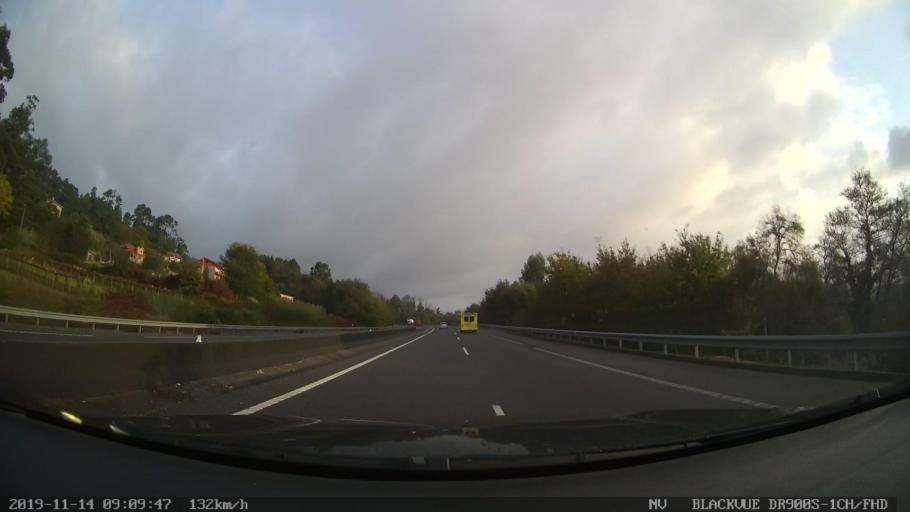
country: ES
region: Galicia
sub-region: Provincia de Pontevedra
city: Porrino
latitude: 42.1723
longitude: -8.6509
